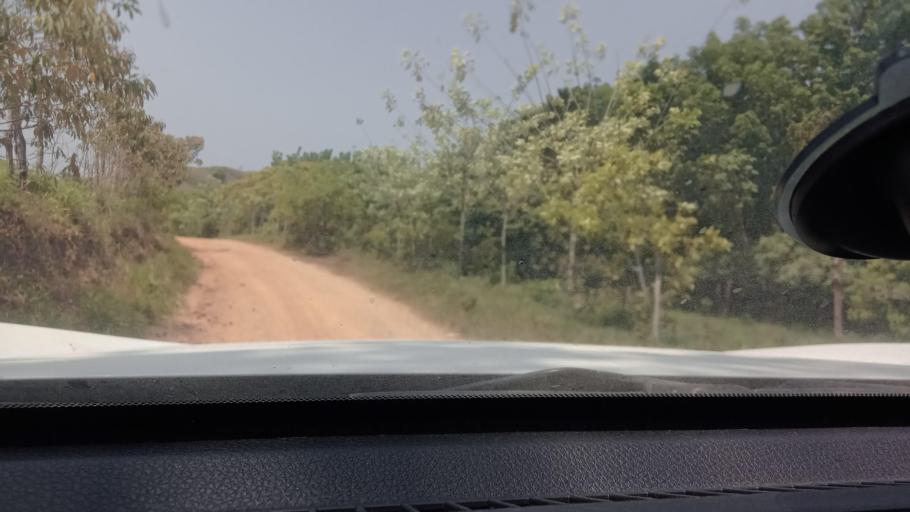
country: MX
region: Tabasco
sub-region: Huimanguillo
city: Francisco Rueda
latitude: 17.4929
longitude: -93.9147
